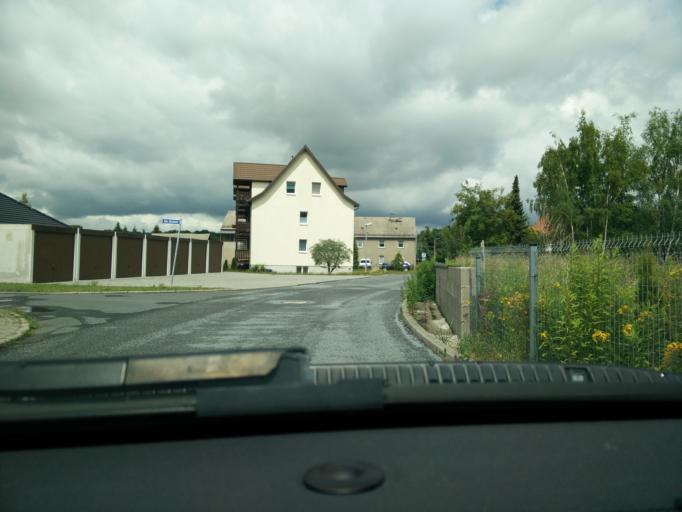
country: DE
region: Saxony
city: Bad Lausick
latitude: 51.1475
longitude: 12.6436
